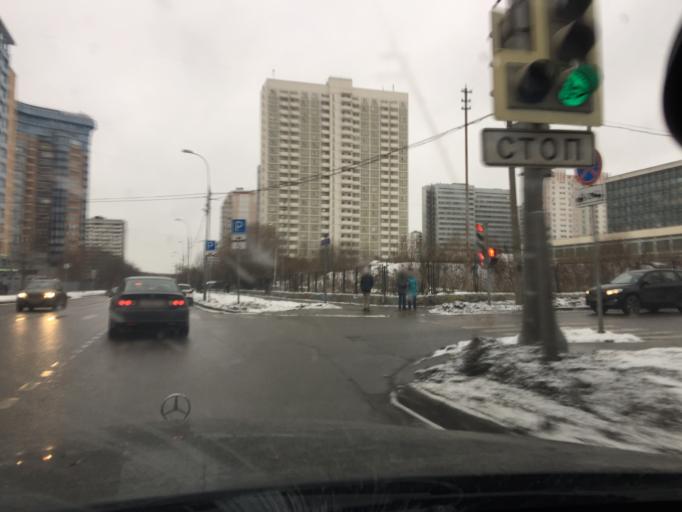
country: RU
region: Moscow
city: Troparevo
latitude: 55.6554
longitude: 37.4778
